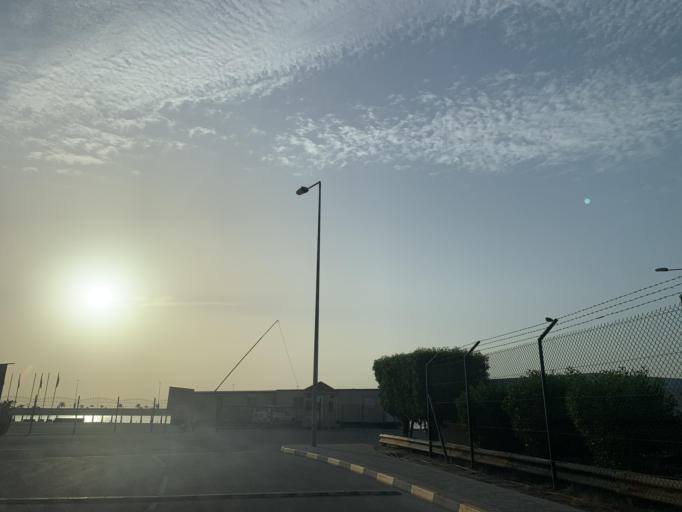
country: BH
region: Manama
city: Manama
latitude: 26.1889
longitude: 50.5850
